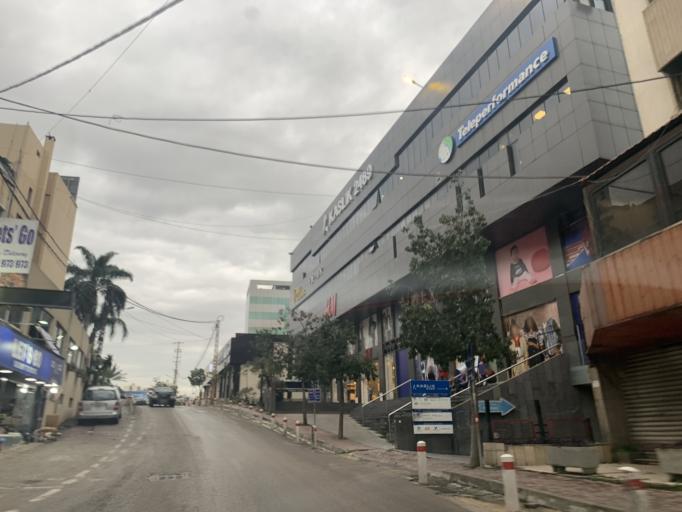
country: LB
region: Mont-Liban
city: Djounie
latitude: 33.9767
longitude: 35.6140
